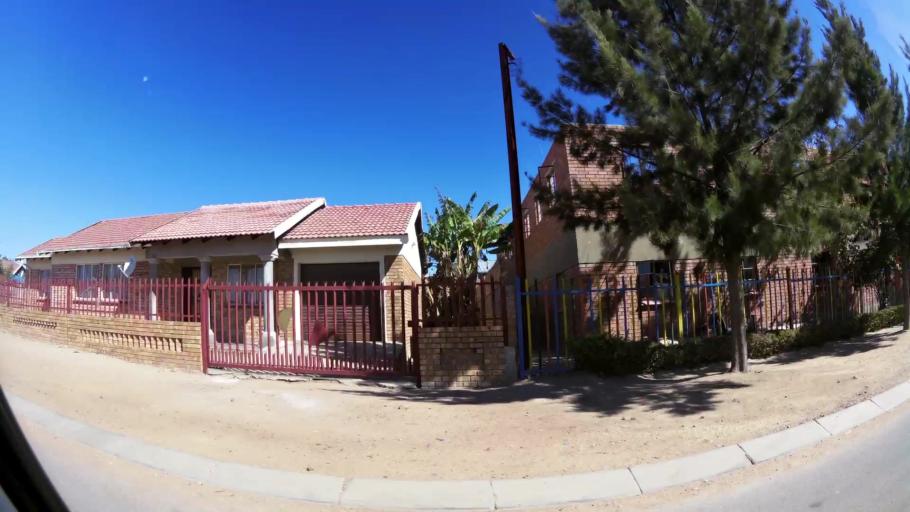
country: ZA
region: Limpopo
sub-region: Capricorn District Municipality
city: Polokwane
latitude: -23.8659
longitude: 29.4249
